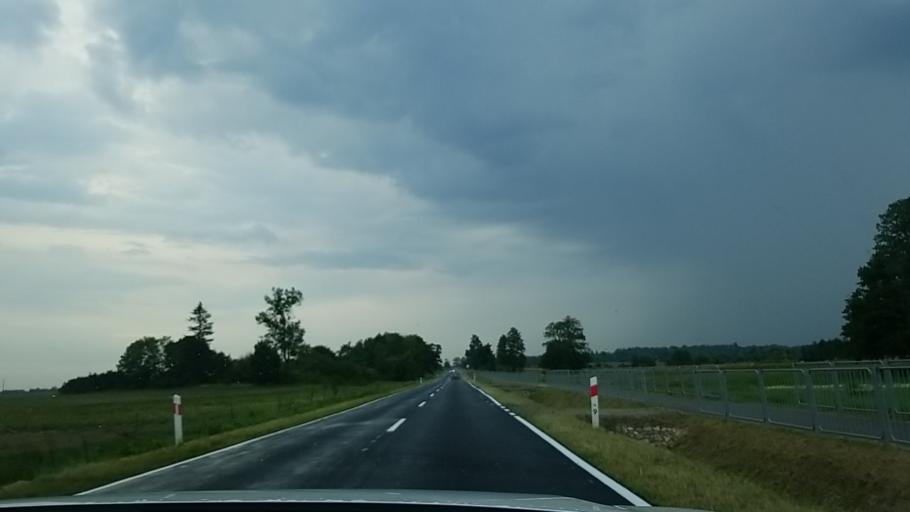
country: PL
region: Lublin Voivodeship
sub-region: Powiat wlodawski
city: Wlodawa
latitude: 51.5950
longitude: 23.5361
